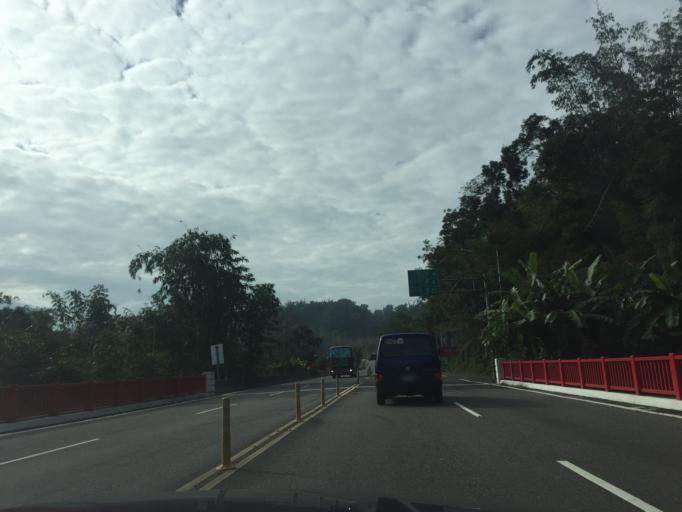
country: TW
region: Taiwan
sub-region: Nantou
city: Puli
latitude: 23.8549
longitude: 120.9019
